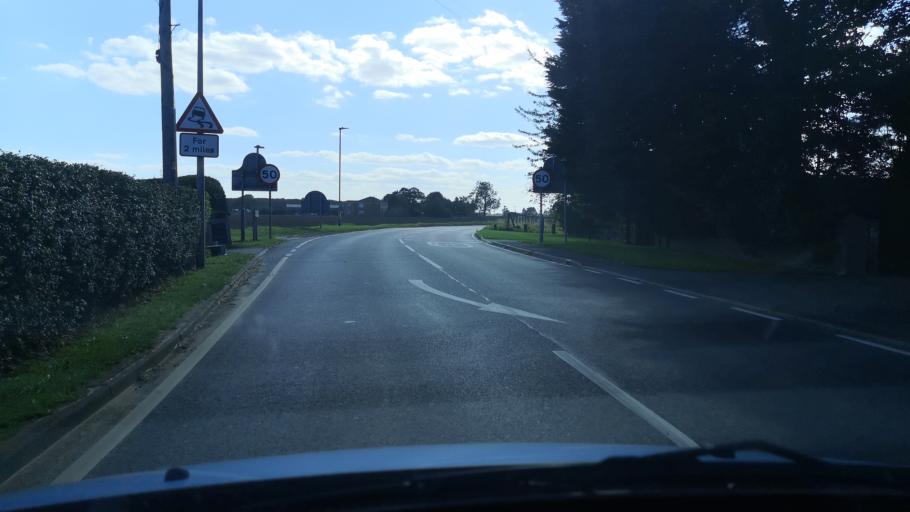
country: GB
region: England
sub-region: North Lincolnshire
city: Eastoft
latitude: 53.6334
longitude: -0.7898
